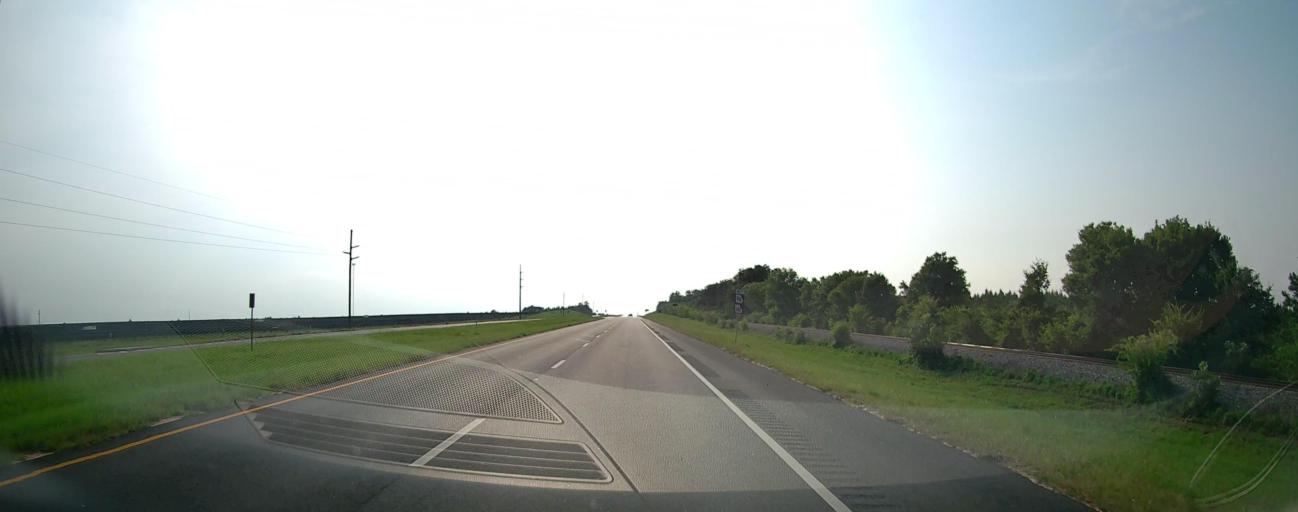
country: US
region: Georgia
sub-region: Taylor County
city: Butler
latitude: 32.5778
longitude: -84.3119
